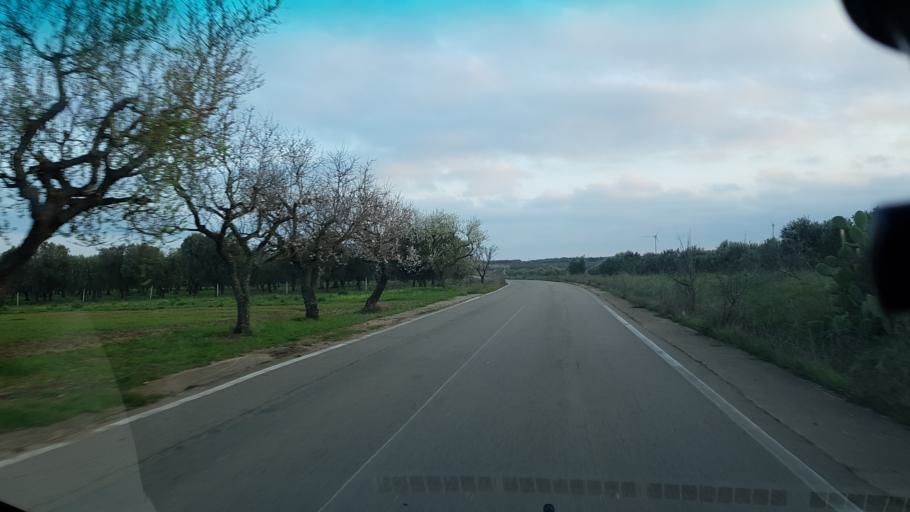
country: IT
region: Apulia
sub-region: Provincia di Brindisi
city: Mesagne
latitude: 40.6231
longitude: 17.7839
